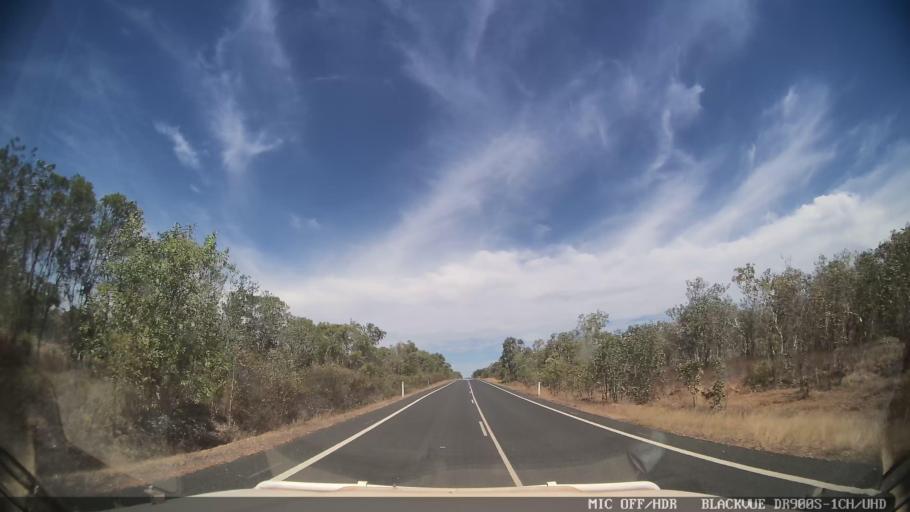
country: AU
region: Queensland
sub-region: Cook
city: Cooktown
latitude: -15.8775
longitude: 144.8605
